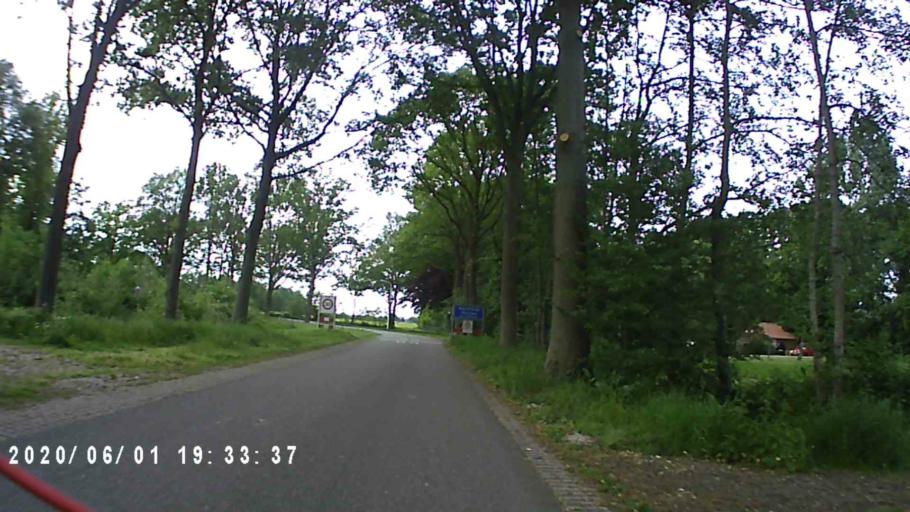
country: NL
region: Friesland
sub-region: Gemeente Achtkarspelen
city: Augustinusga
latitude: 53.2150
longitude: 6.1574
